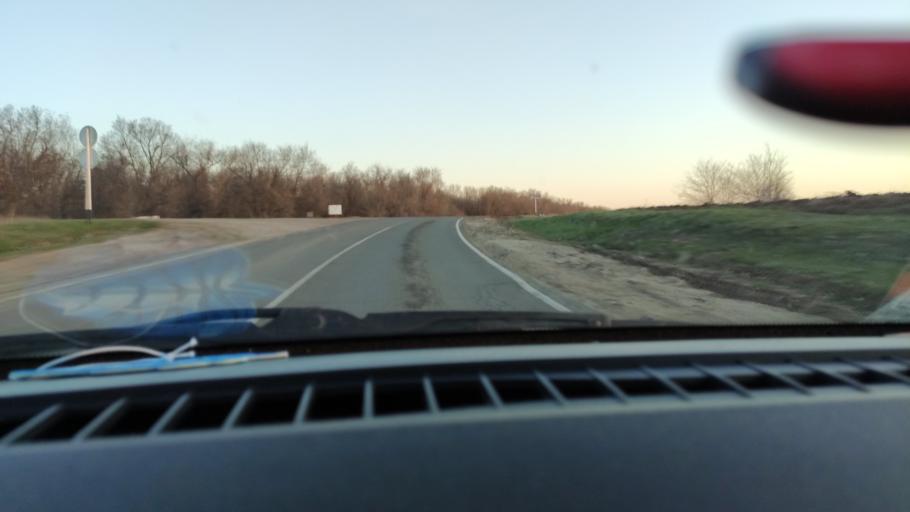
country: RU
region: Saratov
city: Privolzhskiy
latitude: 51.3426
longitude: 46.0415
